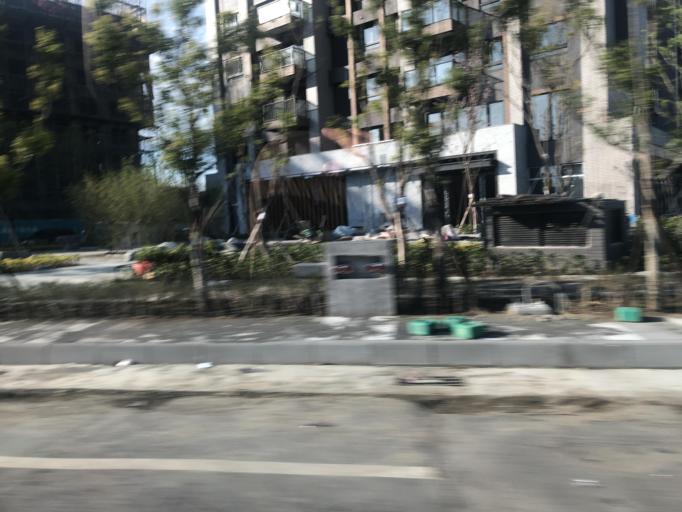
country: TW
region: Taiwan
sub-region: Tainan
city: Tainan
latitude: 23.0303
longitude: 120.1950
